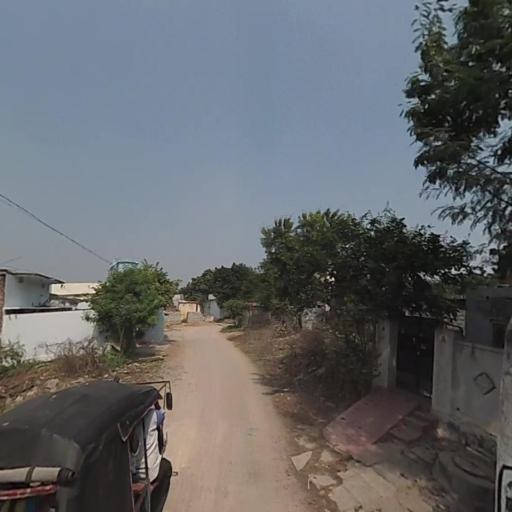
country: IN
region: Telangana
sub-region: Nalgonda
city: Nalgonda
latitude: 17.1855
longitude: 79.1261
